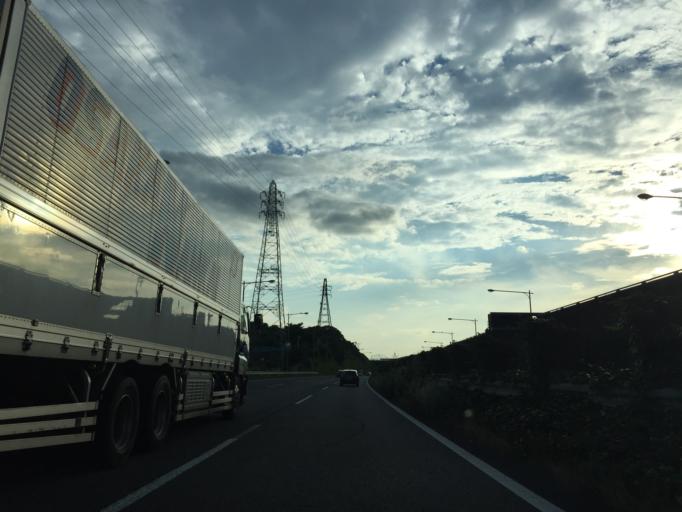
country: JP
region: Kanagawa
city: Hadano
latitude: 35.3508
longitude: 139.2297
